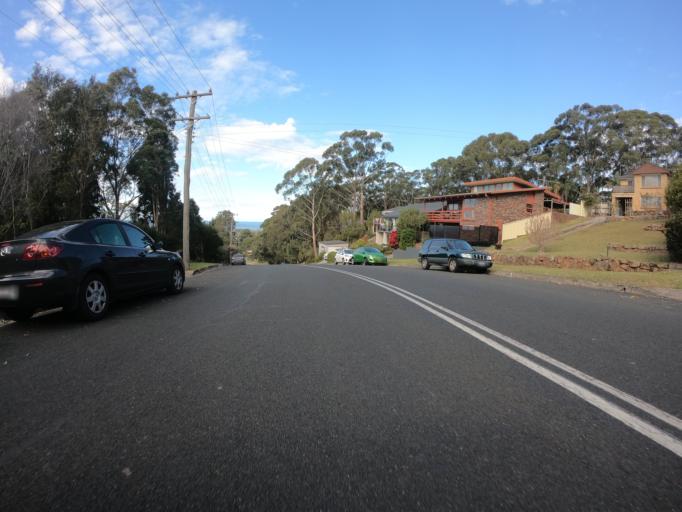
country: AU
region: New South Wales
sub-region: Wollongong
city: Bulli
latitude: -34.3349
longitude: 150.9047
